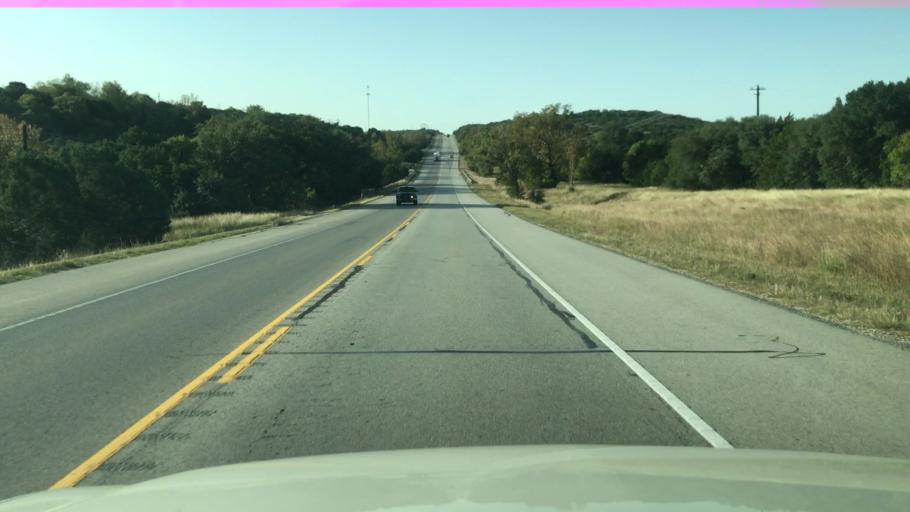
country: US
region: Texas
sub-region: Blanco County
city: Johnson City
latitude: 30.1874
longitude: -98.3783
